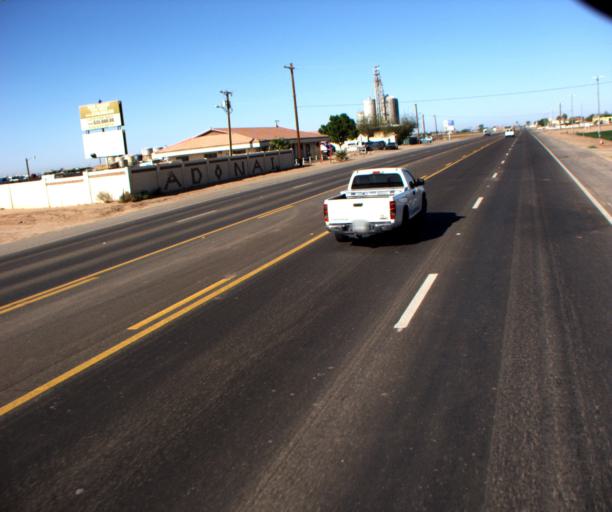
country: US
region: Arizona
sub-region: Yuma County
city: Somerton
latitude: 32.5968
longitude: -114.6858
